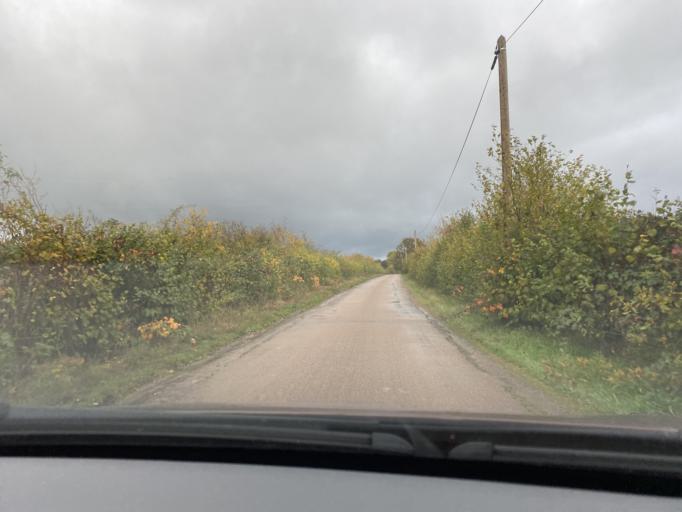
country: FR
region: Bourgogne
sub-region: Departement de la Cote-d'Or
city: Saulieu
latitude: 47.2815
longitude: 4.2023
